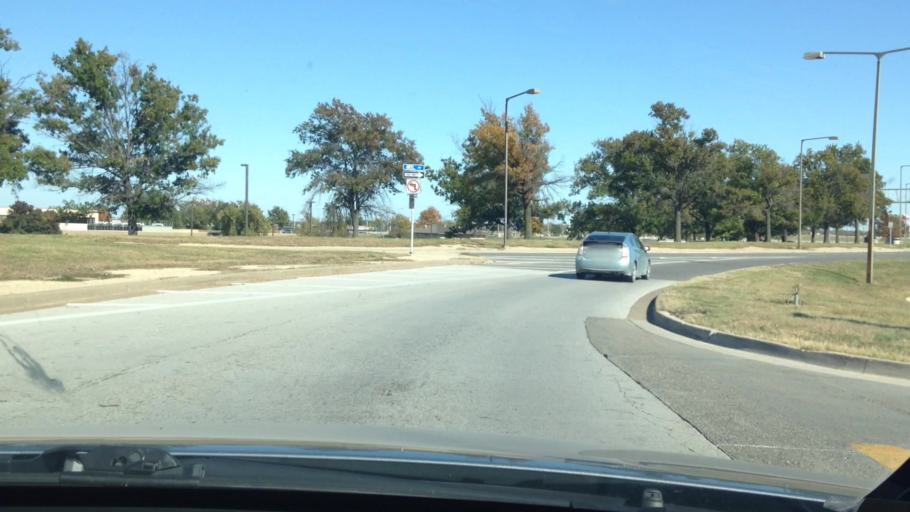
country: US
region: Missouri
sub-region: Platte County
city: Weatherby Lake
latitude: 39.2961
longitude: -94.7174
